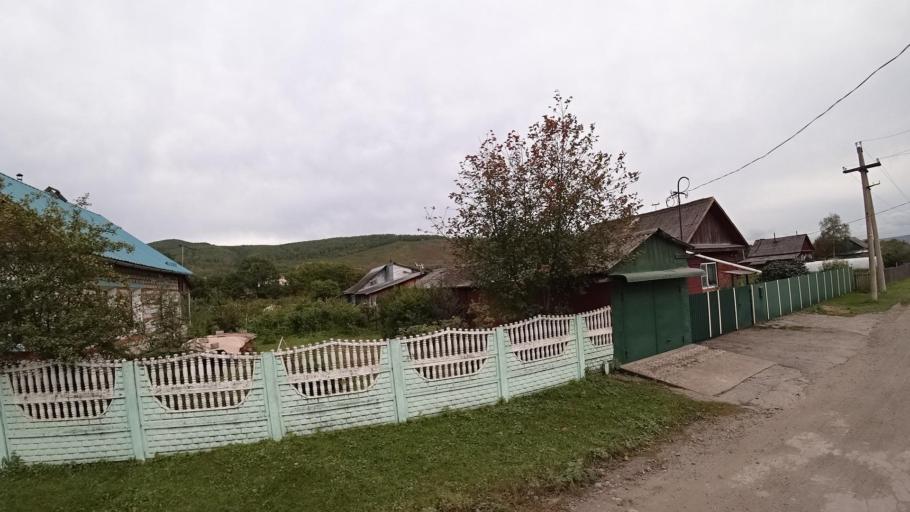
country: RU
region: Jewish Autonomous Oblast
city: Khingansk
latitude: 49.0361
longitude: 131.0495
